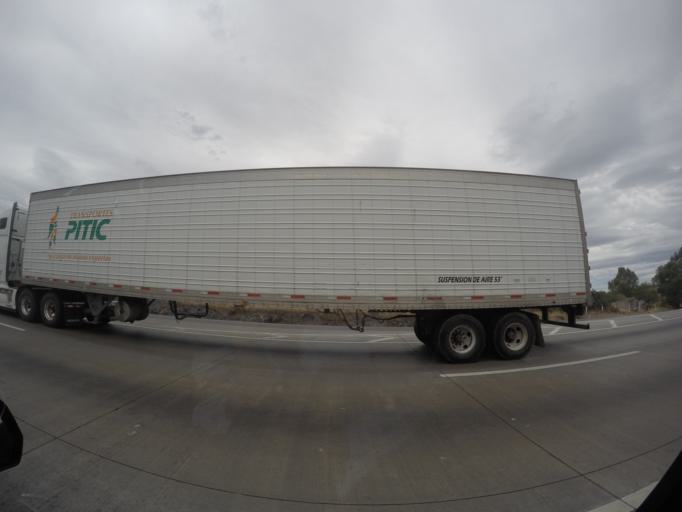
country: MX
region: Hidalgo
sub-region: Tepeji del Rio de Ocampo
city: Santiago Tlautla
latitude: 19.9810
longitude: -99.4373
